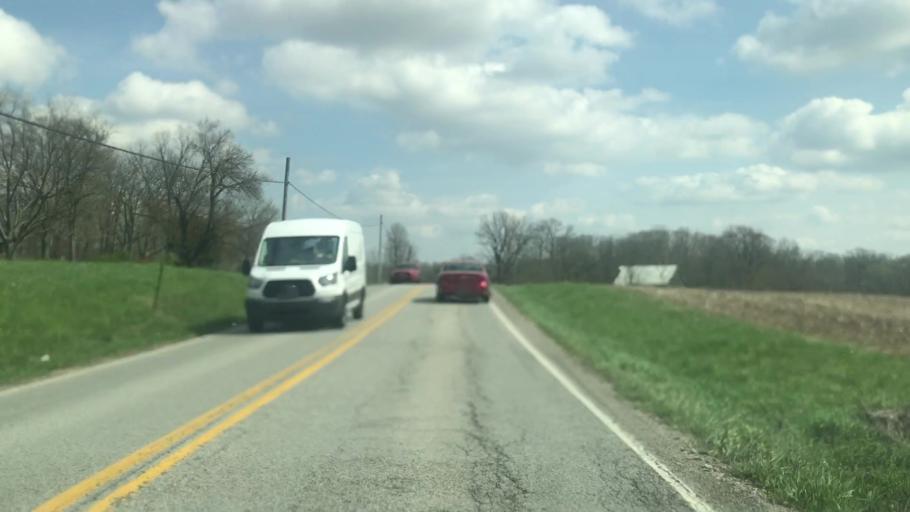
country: US
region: Indiana
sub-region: Johnson County
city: Waterloo
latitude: 39.5549
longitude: -86.2182
